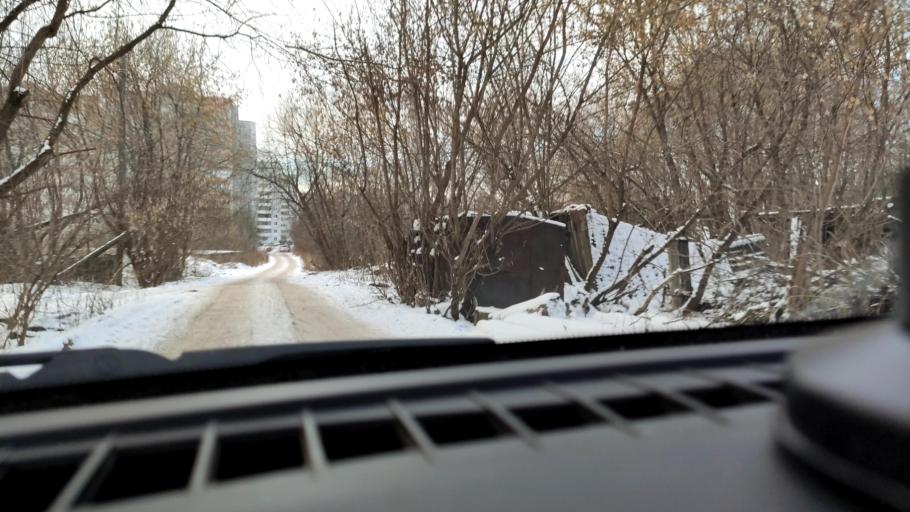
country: RU
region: Perm
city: Froly
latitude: 57.9458
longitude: 56.2795
